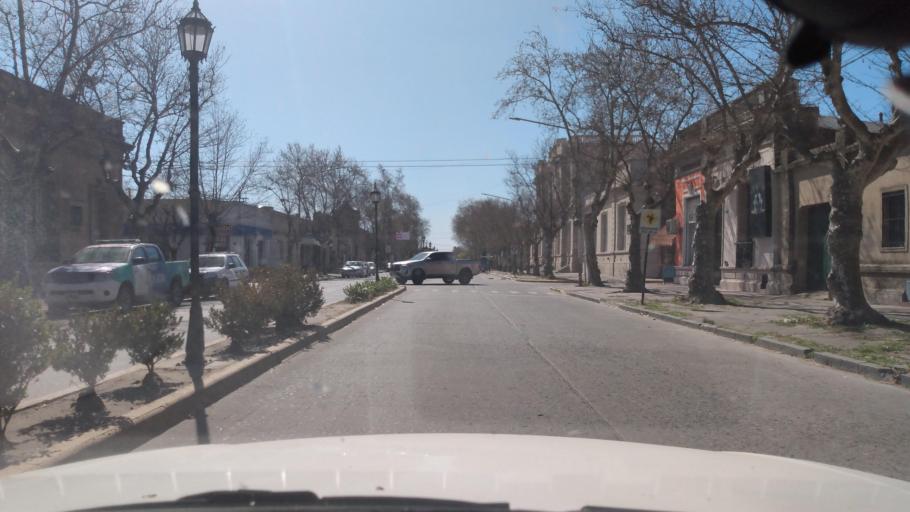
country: AR
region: Buenos Aires
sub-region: Partido de Mercedes
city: Mercedes
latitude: -34.6464
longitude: -59.4305
